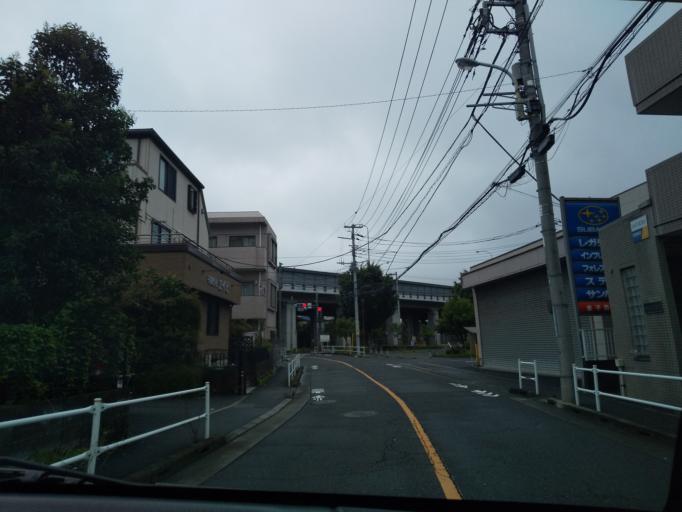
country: JP
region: Tokyo
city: Hino
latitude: 35.6752
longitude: 139.4164
